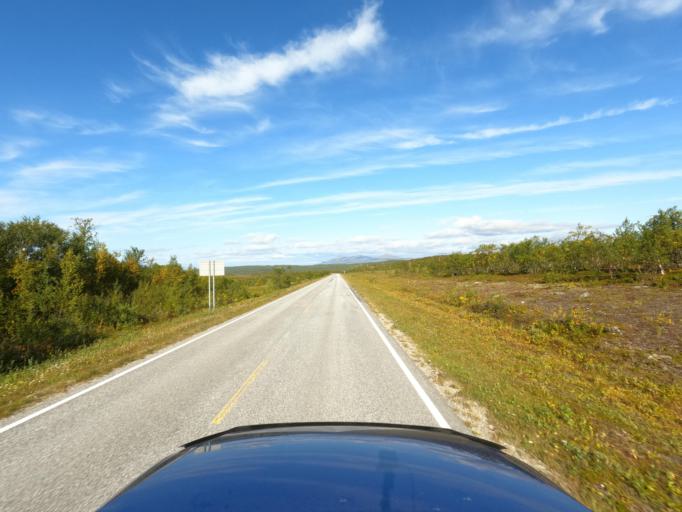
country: NO
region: Finnmark Fylke
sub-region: Karasjok
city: Karasjohka
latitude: 69.7289
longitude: 25.2345
